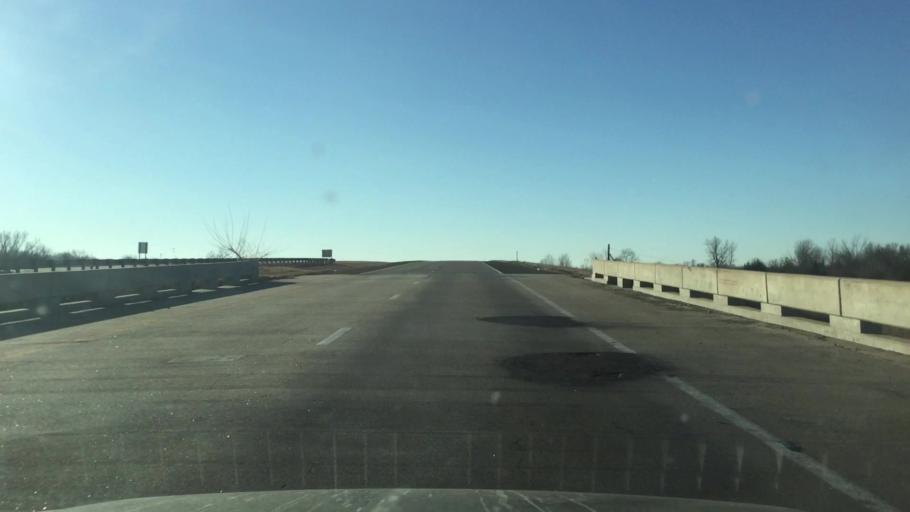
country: US
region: Kansas
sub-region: Miami County
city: Paola
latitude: 38.6359
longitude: -94.8360
